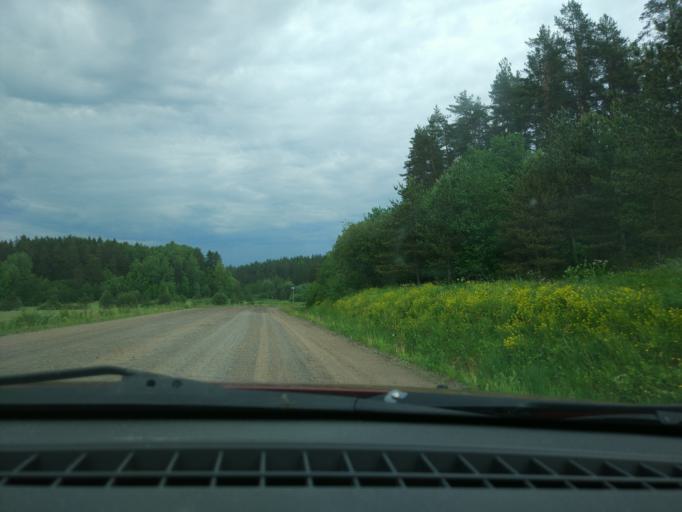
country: RU
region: Leningrad
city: Kuznechnoye
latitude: 61.2807
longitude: 29.8536
